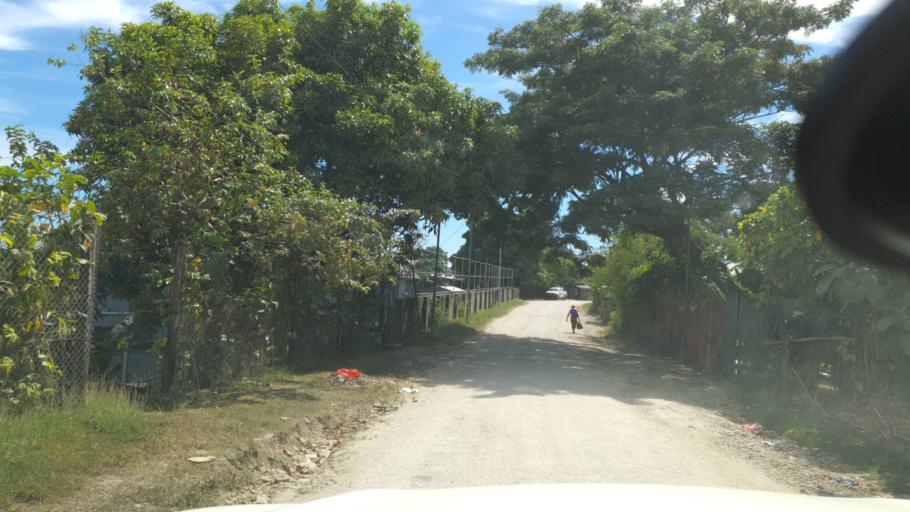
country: SB
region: Guadalcanal
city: Honiara
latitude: -9.4403
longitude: 159.9754
